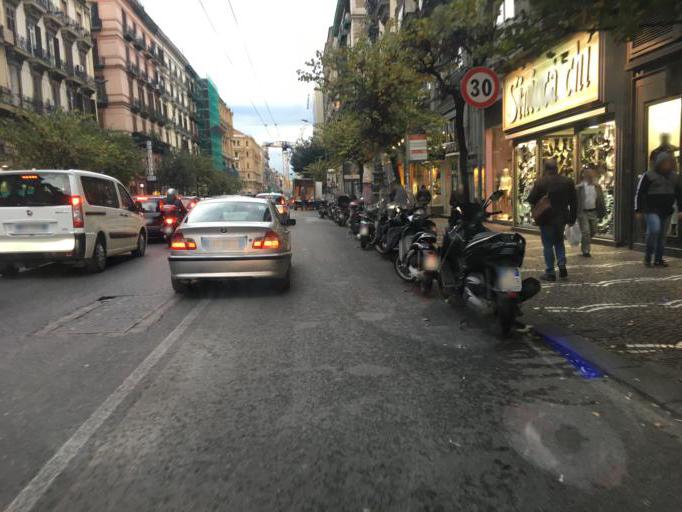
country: IT
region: Campania
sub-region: Provincia di Napoli
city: Napoli
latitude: 40.8489
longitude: 14.2637
